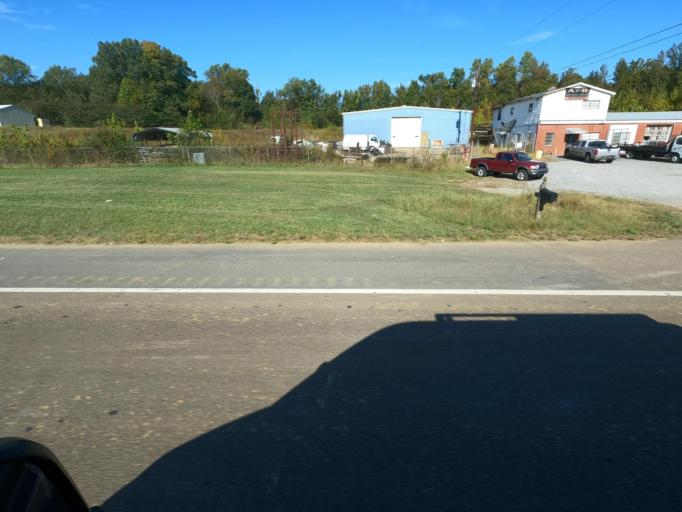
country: US
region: Tennessee
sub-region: Tipton County
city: Munford
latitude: 35.4256
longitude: -89.8132
